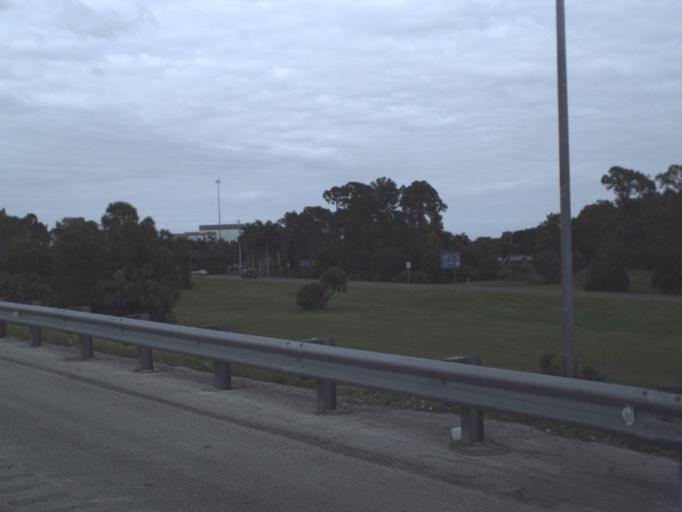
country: US
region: Florida
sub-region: Collier County
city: Vineyards
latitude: 26.2090
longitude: -81.7359
